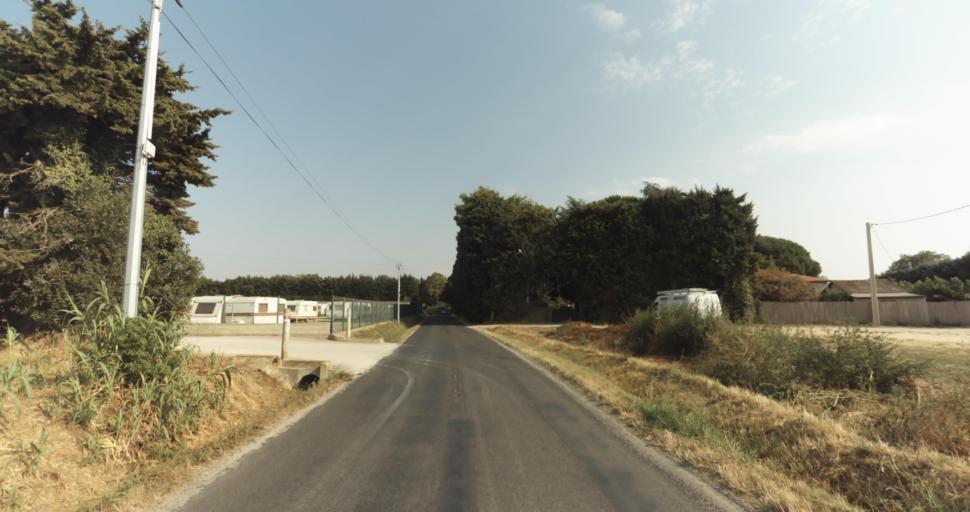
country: FR
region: Languedoc-Roussillon
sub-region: Departement des Pyrenees-Orientales
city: Latour-Bas-Elne
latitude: 42.6026
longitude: 3.0067
